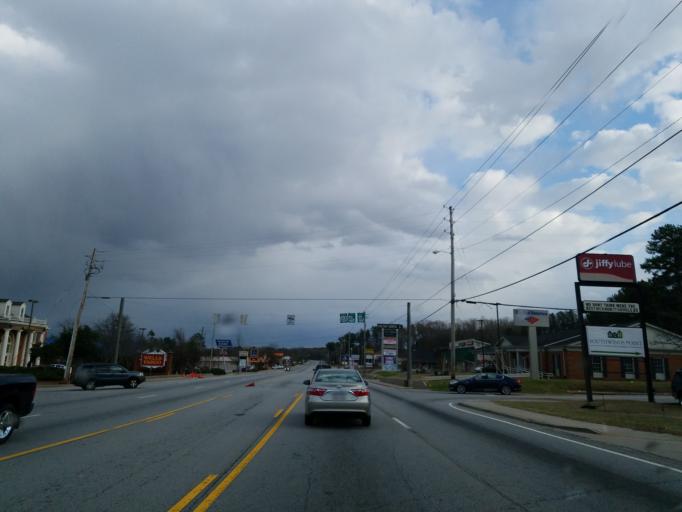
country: US
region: Georgia
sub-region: Henry County
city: Stockbridge
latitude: 33.5517
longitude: -84.2576
